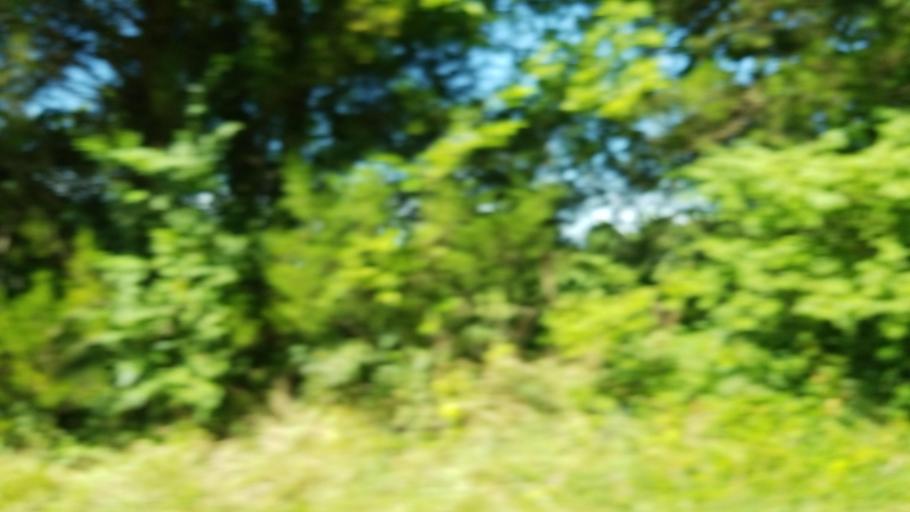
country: US
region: Illinois
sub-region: Williamson County
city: Johnston City
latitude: 37.7845
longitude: -88.8198
